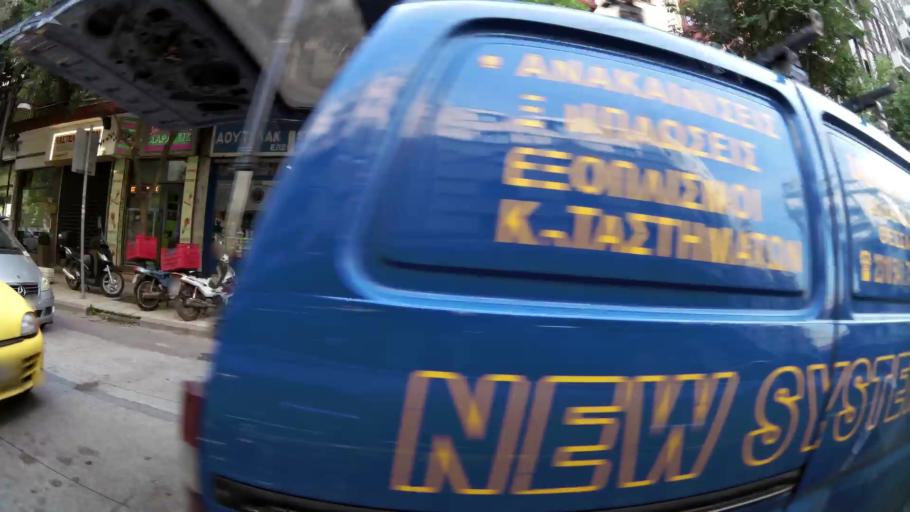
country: GR
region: Central Macedonia
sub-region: Nomos Thessalonikis
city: Thessaloniki
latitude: 40.6395
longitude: 22.9361
